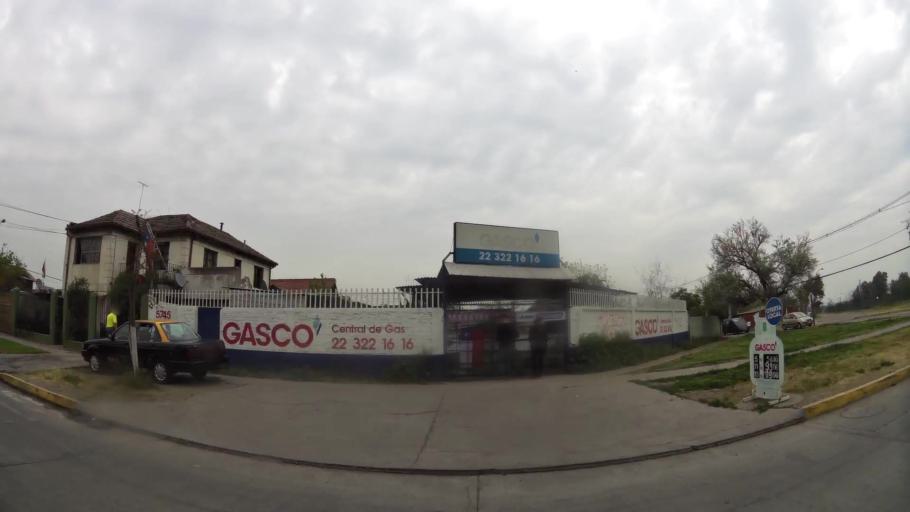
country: CL
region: Santiago Metropolitan
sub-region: Provincia de Santiago
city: Villa Presidente Frei, Nunoa, Santiago, Chile
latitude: -33.5053
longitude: -70.5965
